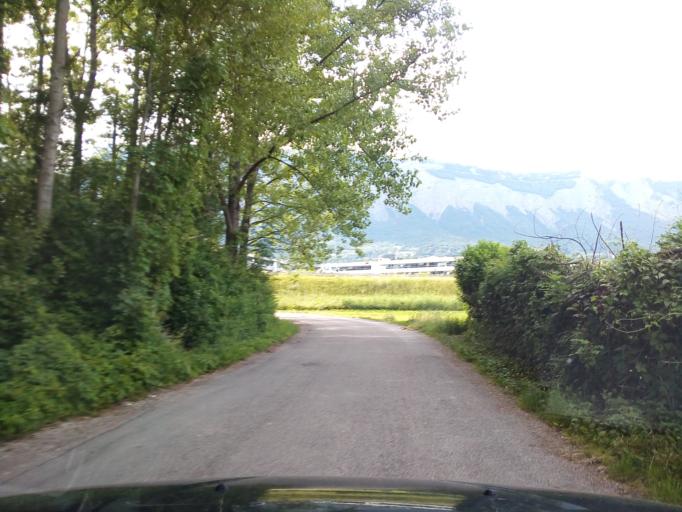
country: FR
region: Rhone-Alpes
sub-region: Departement de l'Isere
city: Montbonnot-Saint-Martin
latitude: 45.2118
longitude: 5.8107
